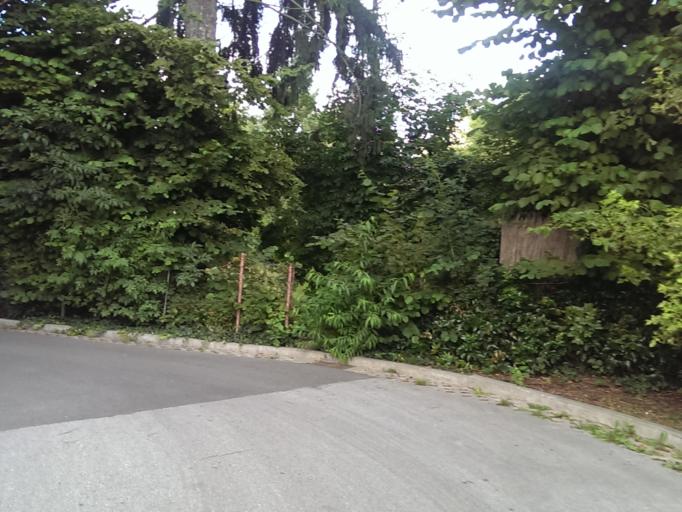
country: AT
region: Styria
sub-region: Graz Stadt
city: Graz
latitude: 47.0656
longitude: 15.4606
